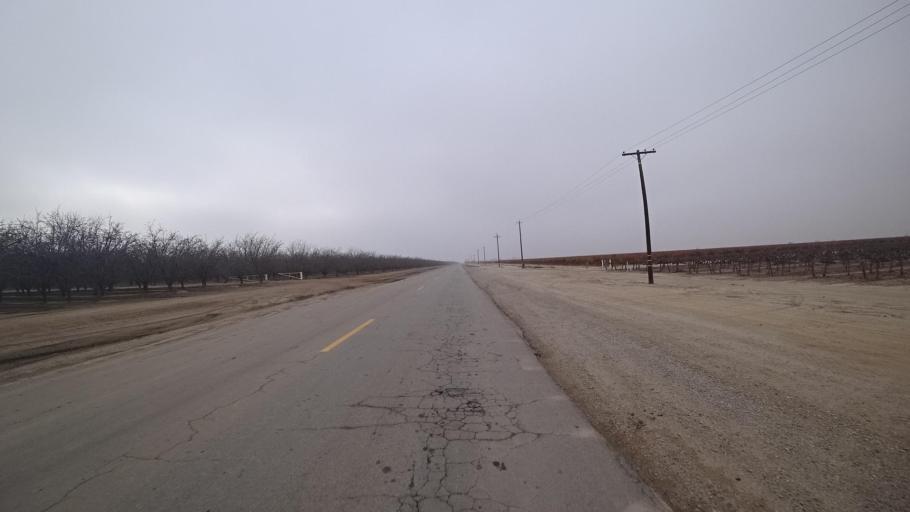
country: US
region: California
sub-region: Kern County
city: Maricopa
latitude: 35.0938
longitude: -119.2247
